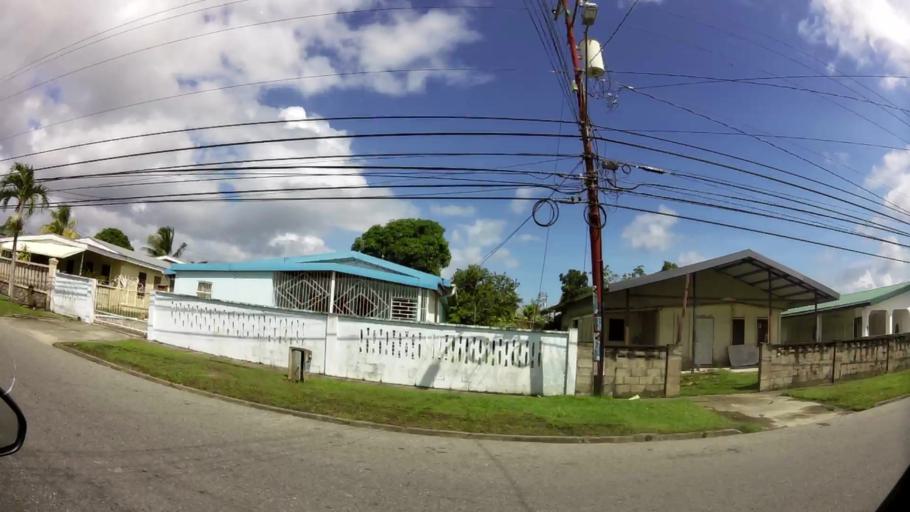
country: TT
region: Borough of Arima
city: Arima
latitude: 10.6201
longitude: -61.2629
